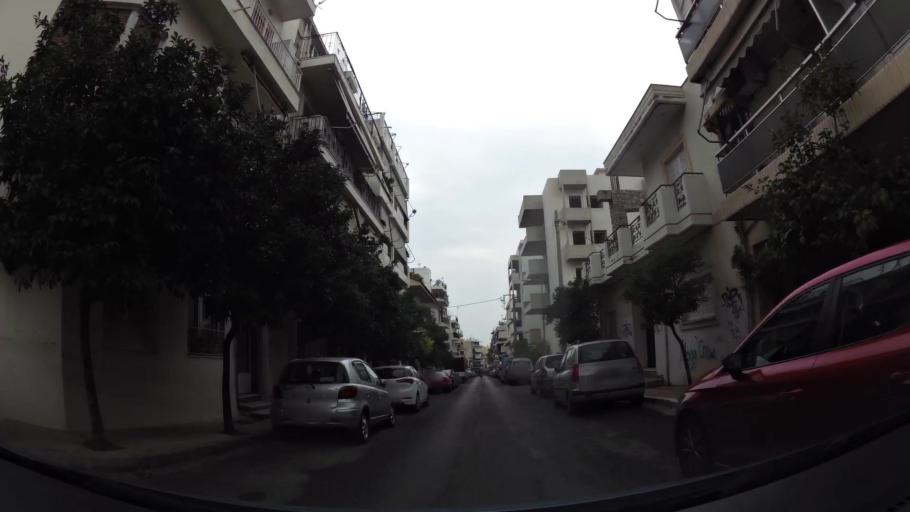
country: GR
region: Attica
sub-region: Nomarchia Athinas
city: Kaisariani
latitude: 37.9577
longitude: 23.7641
